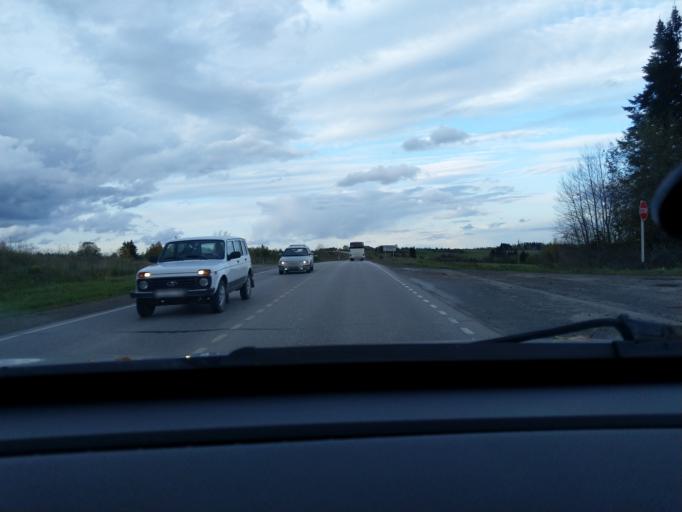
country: RU
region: Perm
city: Polazna
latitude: 58.3520
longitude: 56.4726
